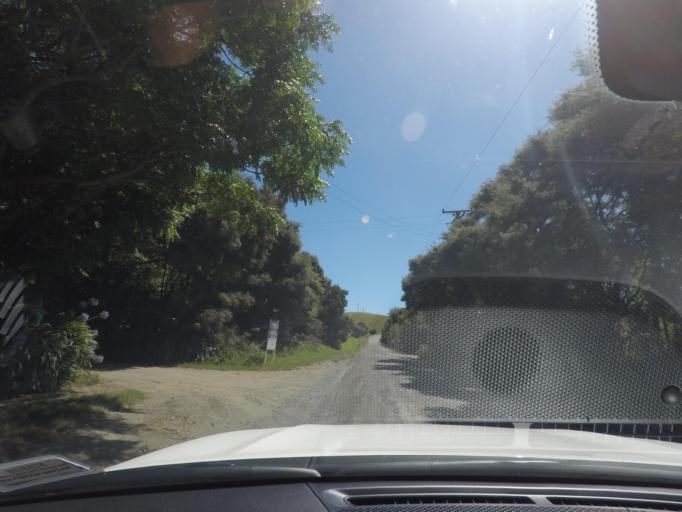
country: NZ
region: Auckland
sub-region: Auckland
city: Parakai
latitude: -36.5815
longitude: 174.3142
